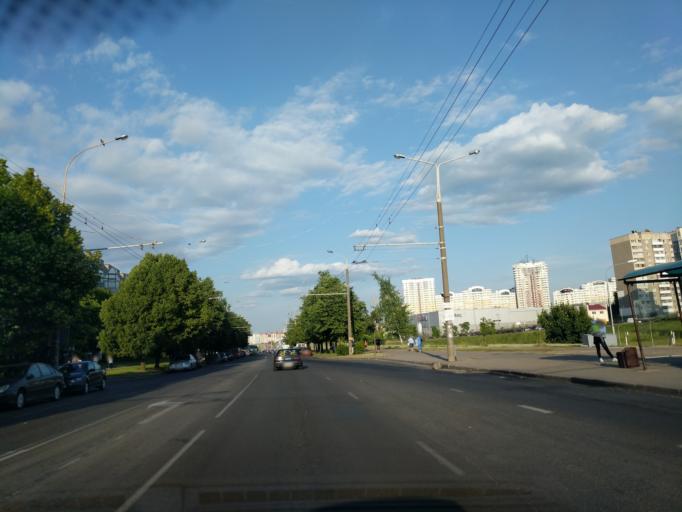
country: BY
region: Minsk
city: Malinovka
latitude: 53.8491
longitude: 27.4653
